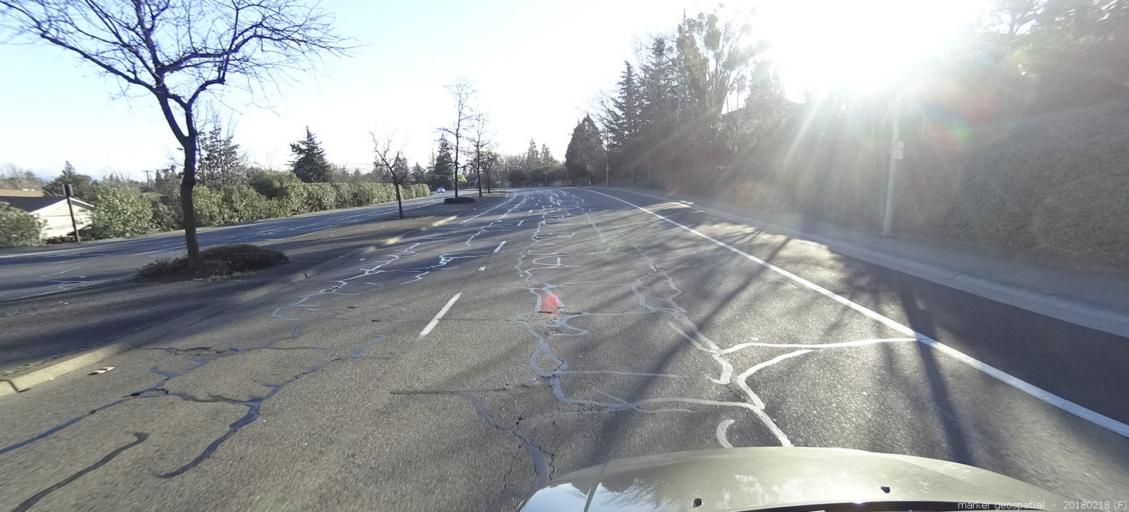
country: US
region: California
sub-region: Sacramento County
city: Orangevale
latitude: 38.6638
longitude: -121.2177
